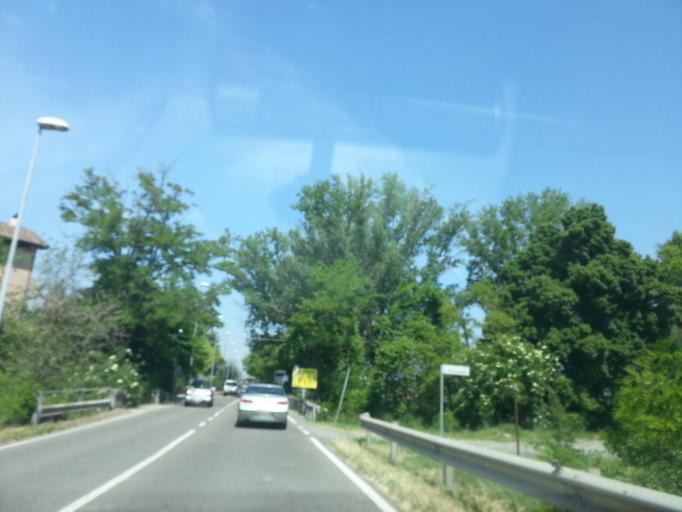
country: IT
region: Emilia-Romagna
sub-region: Provincia di Reggio Emilia
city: Fogliano
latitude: 44.6627
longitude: 10.6450
